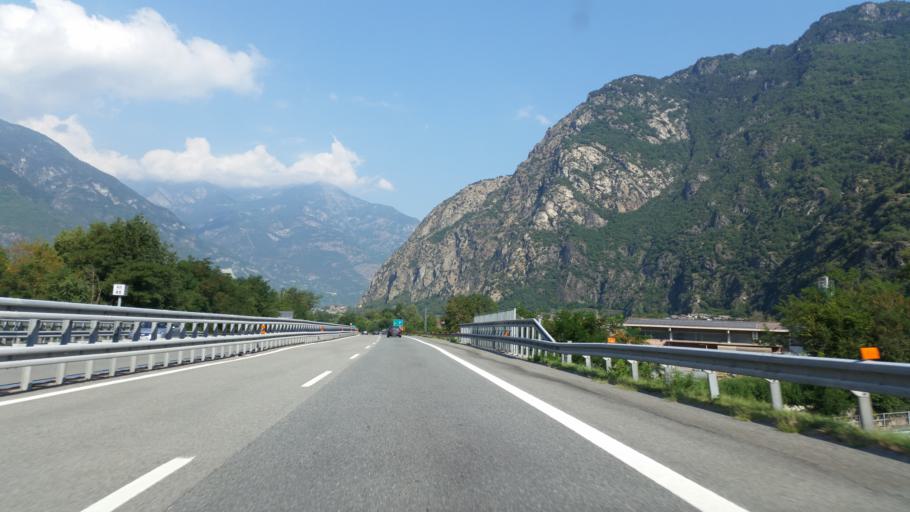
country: IT
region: Aosta Valley
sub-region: Valle d'Aosta
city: Arnad
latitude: 45.6400
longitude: 7.7206
